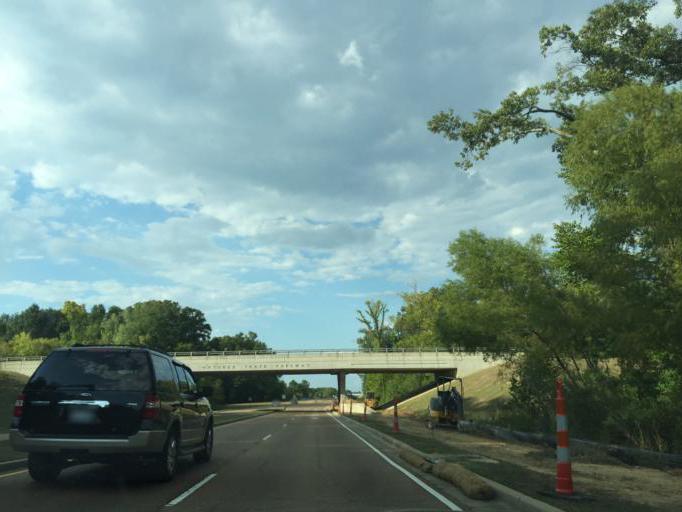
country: US
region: Mississippi
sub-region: Madison County
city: Ridgeland
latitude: 32.4262
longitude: -90.1063
